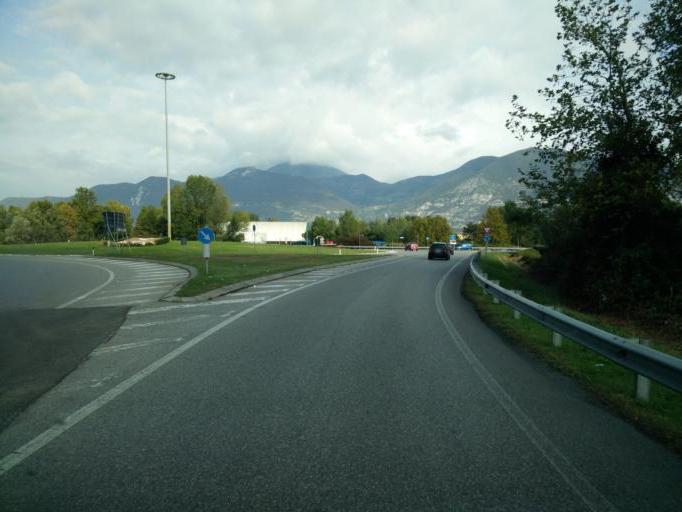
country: IT
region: Lombardy
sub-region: Provincia di Brescia
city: Iseo
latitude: 45.6501
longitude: 10.0427
